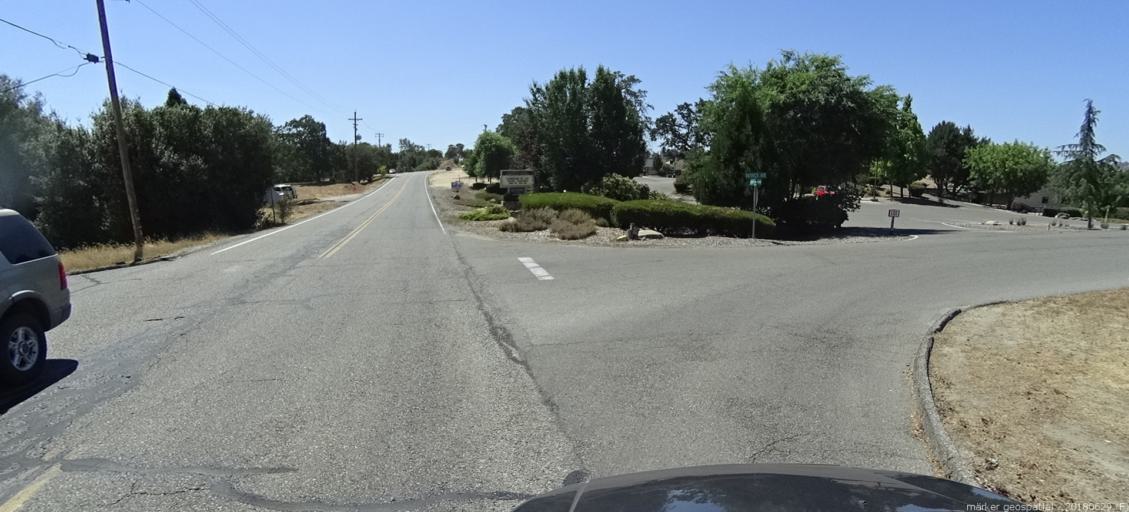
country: US
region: California
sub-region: Madera County
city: Yosemite Lakes
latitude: 37.1653
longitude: -119.7517
